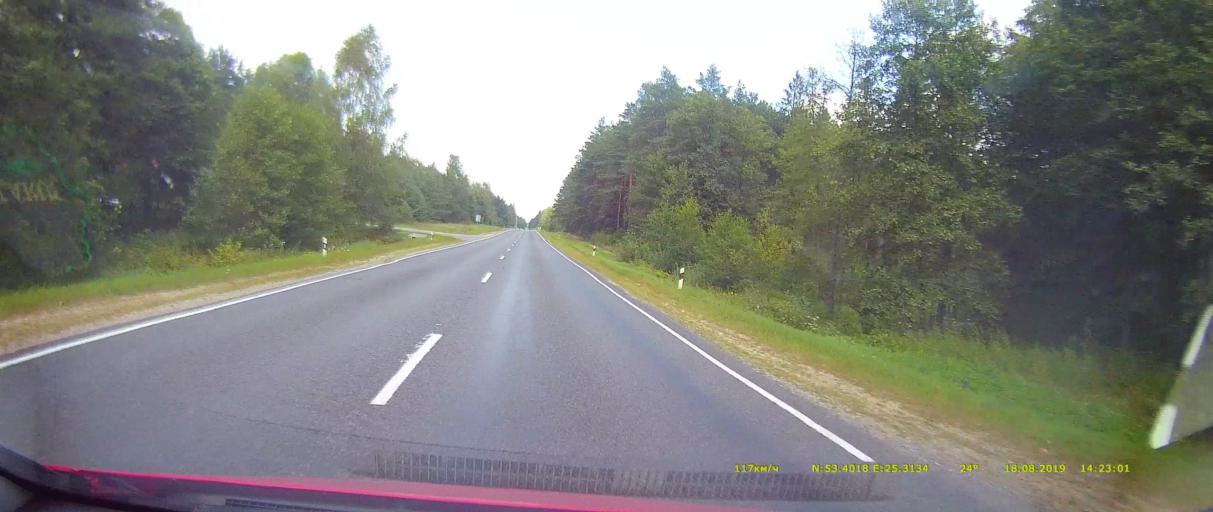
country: BY
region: Grodnenskaya
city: Dzyatlava
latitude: 53.4214
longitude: 25.3206
